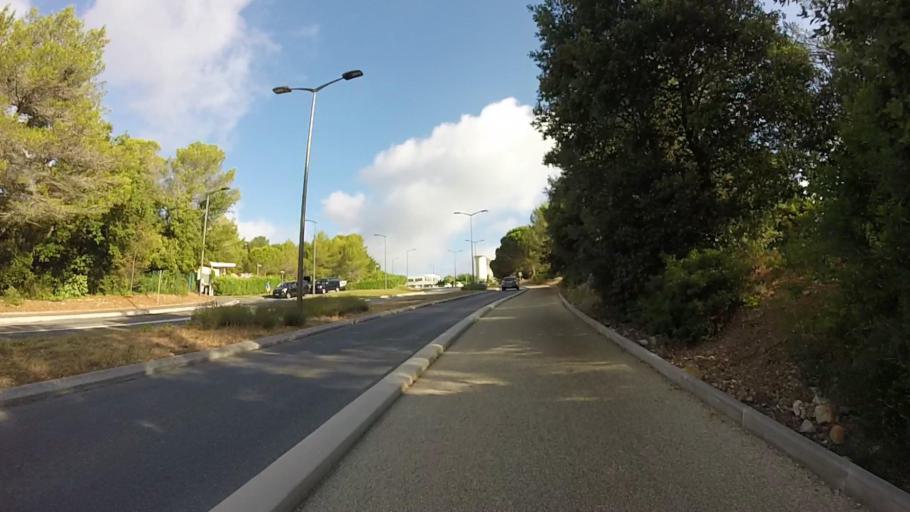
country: FR
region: Provence-Alpes-Cote d'Azur
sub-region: Departement des Alpes-Maritimes
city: Biot
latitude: 43.6224
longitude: 7.0625
